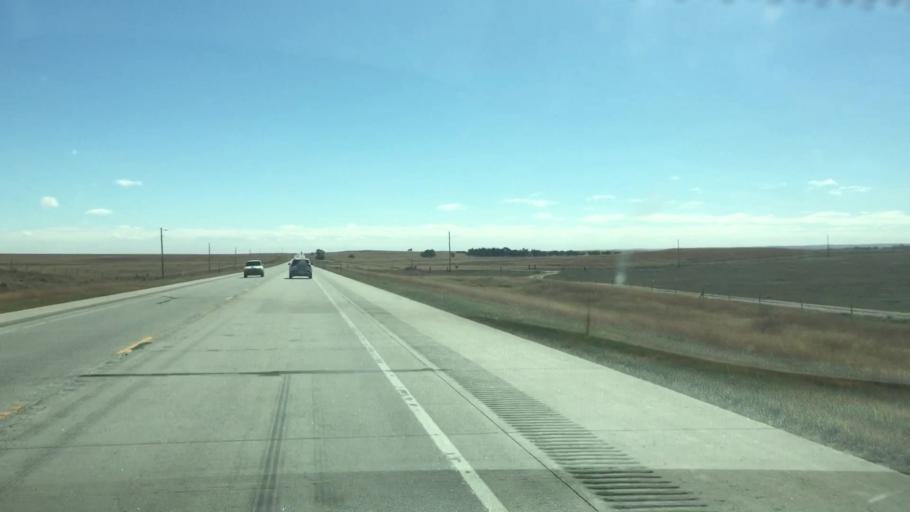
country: US
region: Colorado
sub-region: Lincoln County
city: Limon
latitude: 39.2045
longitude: -103.5862
